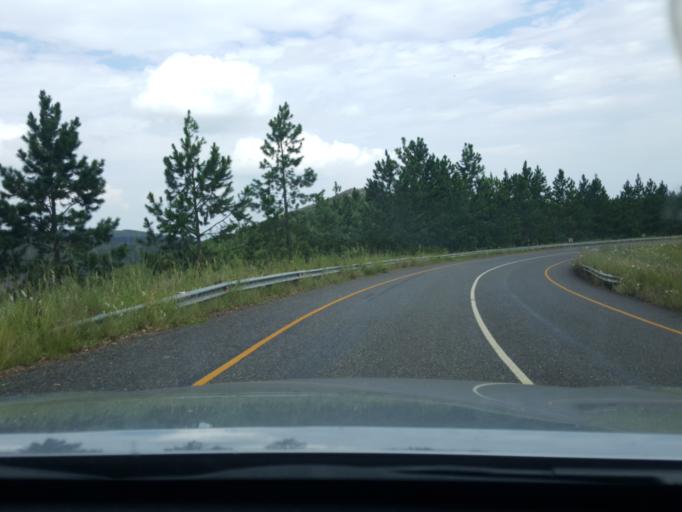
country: ZA
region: Mpumalanga
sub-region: Ehlanzeni District
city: White River
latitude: -25.1686
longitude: 30.8684
